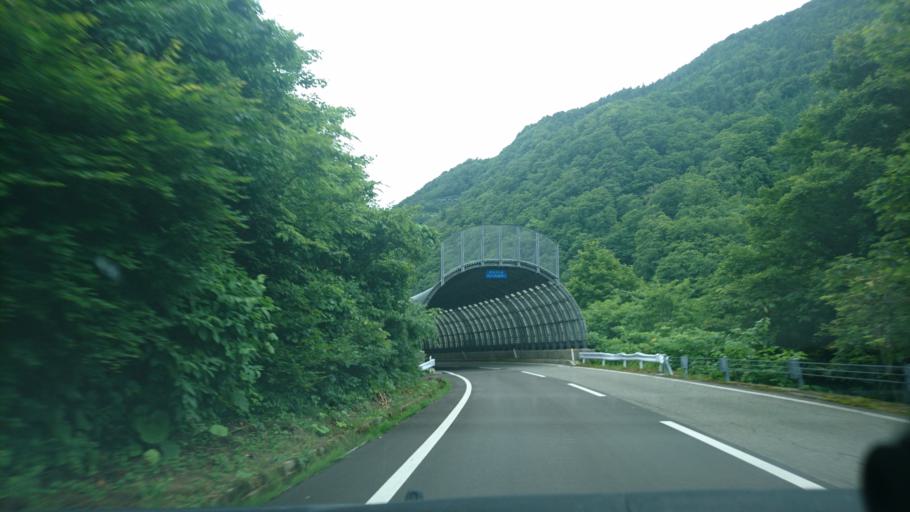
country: JP
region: Akita
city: Yuzawa
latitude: 39.1655
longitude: 140.7481
